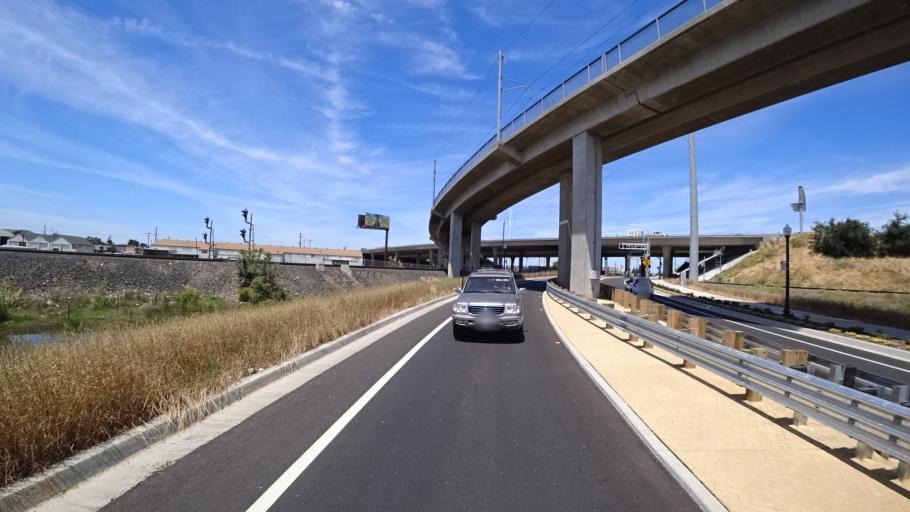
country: US
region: California
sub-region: Sacramento County
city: Florin
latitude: 38.5502
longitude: -121.4205
